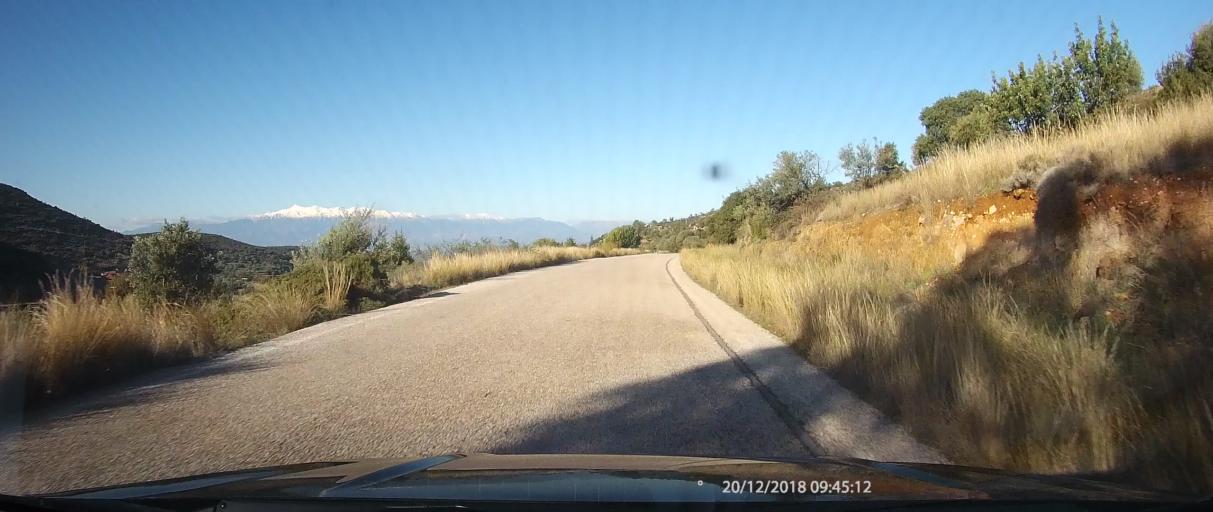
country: GR
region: Peloponnese
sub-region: Nomos Lakonias
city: Yerakion
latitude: 36.9823
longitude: 22.7299
